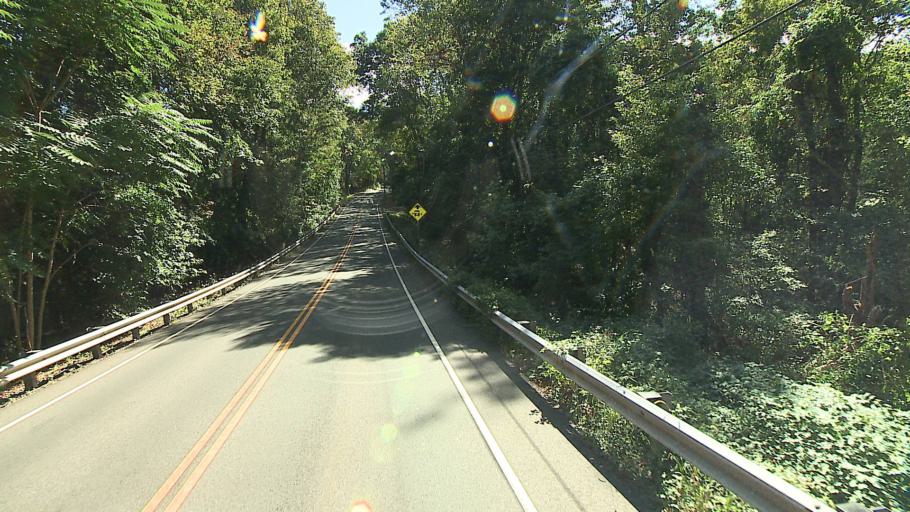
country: US
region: Connecticut
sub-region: Fairfield County
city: Wilton
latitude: 41.1947
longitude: -73.4004
